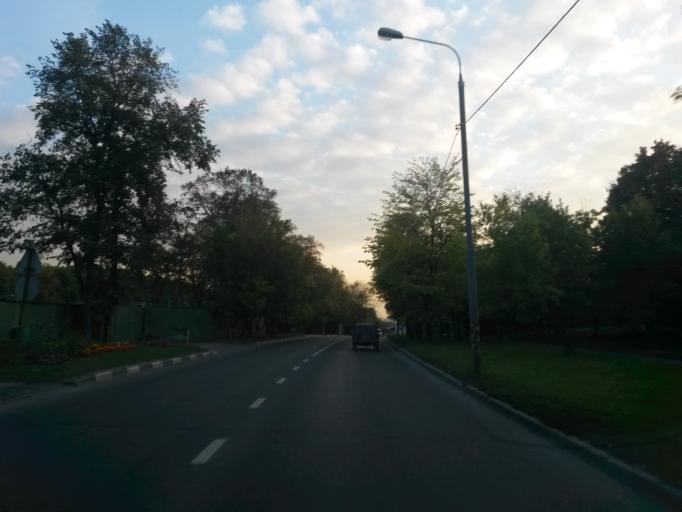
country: RU
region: Moscow
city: Orekhovo-Borisovo Severnoye
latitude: 55.6314
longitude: 37.6843
